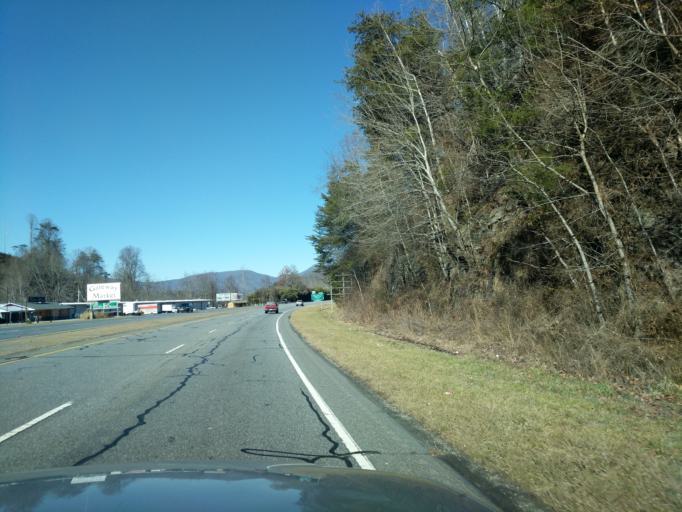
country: US
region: North Carolina
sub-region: Swain County
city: Cherokee
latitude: 35.4084
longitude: -83.3257
